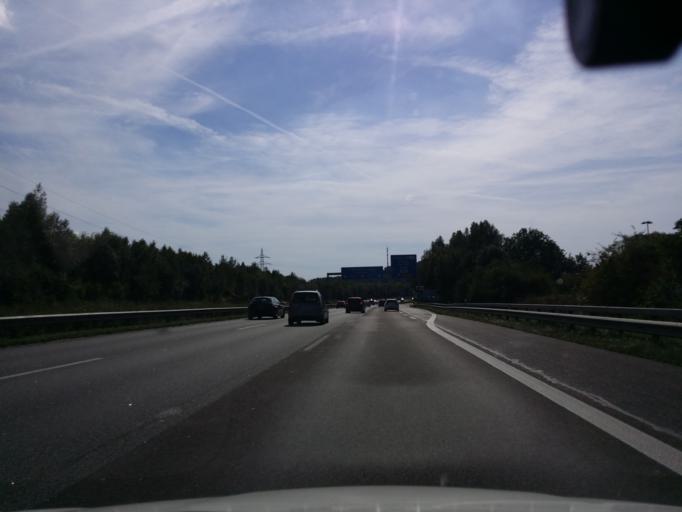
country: DE
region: Rheinland-Pfalz
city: Heiligenroth
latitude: 50.4506
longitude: 7.8564
